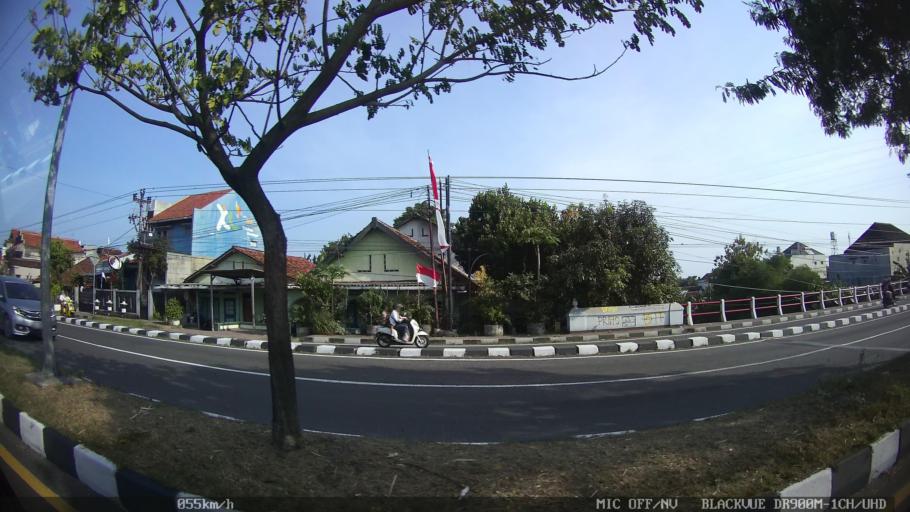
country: ID
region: Daerah Istimewa Yogyakarta
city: Kasihan
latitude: -7.8284
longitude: 110.3496
